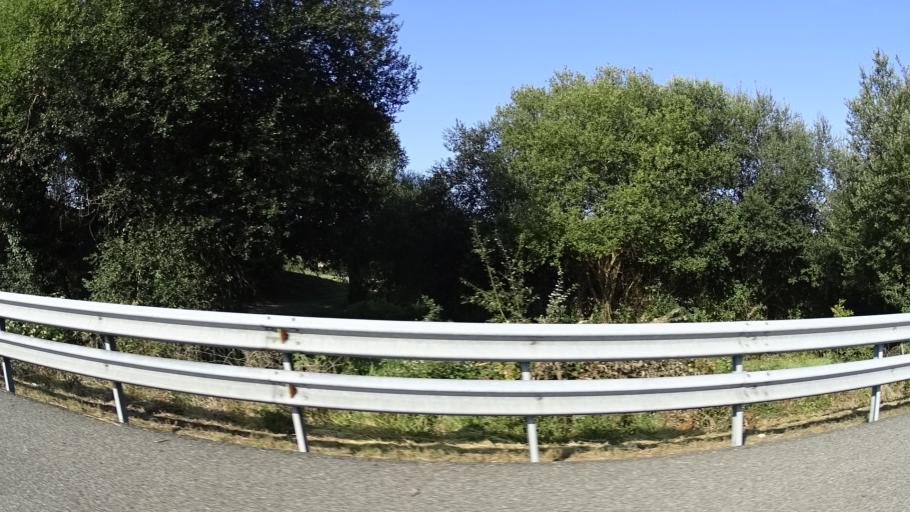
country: ES
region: Galicia
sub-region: Provincia da Coruna
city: Betanzos
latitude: 43.2603
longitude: -8.2545
